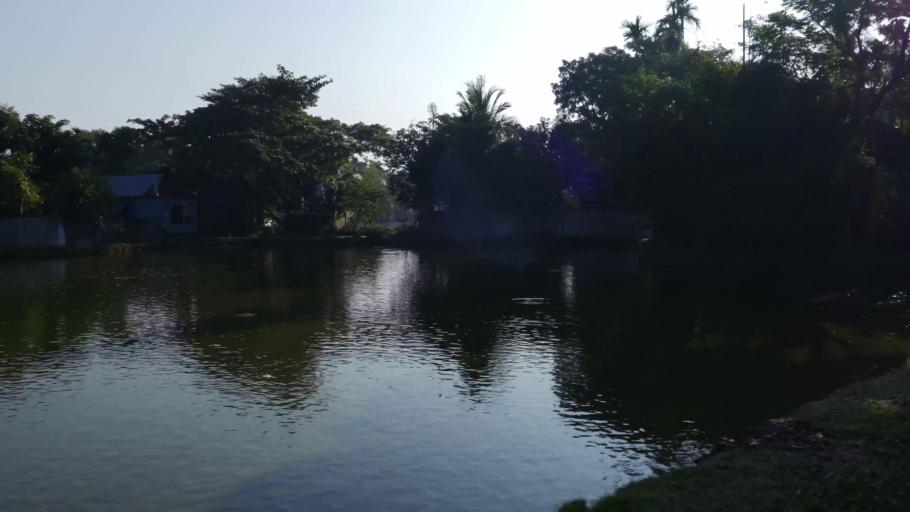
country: BD
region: Dhaka
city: Jamalpur
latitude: 24.8647
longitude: 90.0534
